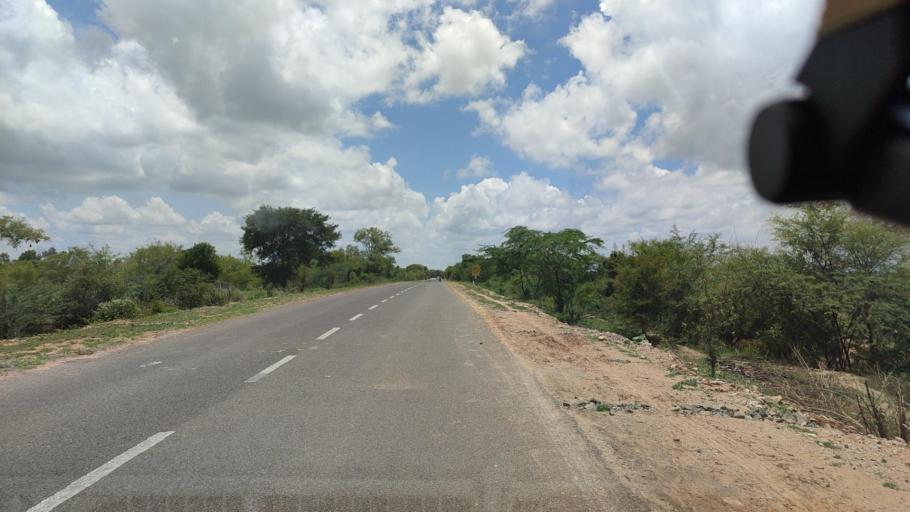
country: MM
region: Magway
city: Taungdwingyi
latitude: 20.1829
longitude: 95.4582
